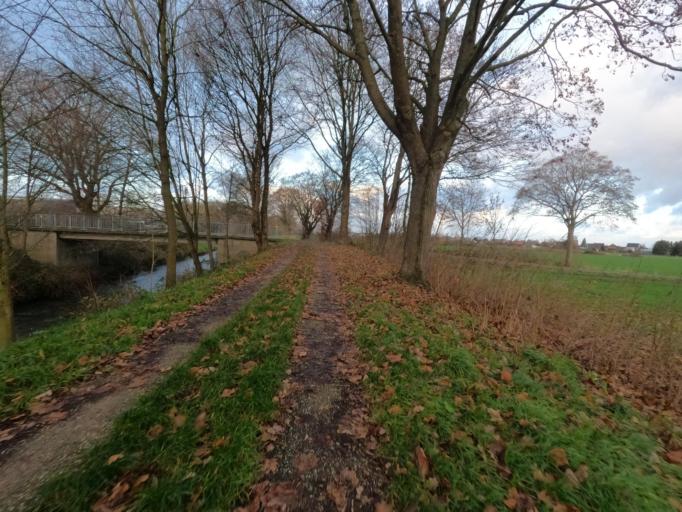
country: DE
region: North Rhine-Westphalia
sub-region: Regierungsbezirk Koln
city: Heinsberg
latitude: 51.0679
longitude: 6.1216
